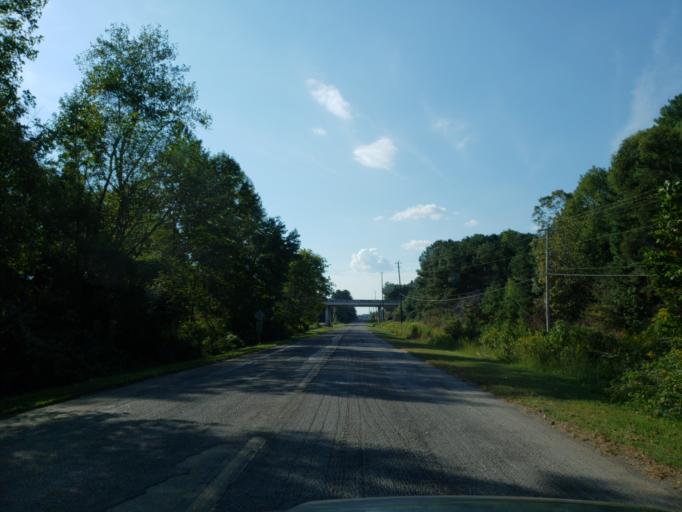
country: US
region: Georgia
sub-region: Cobb County
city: Powder Springs
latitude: 33.8643
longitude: -84.6943
